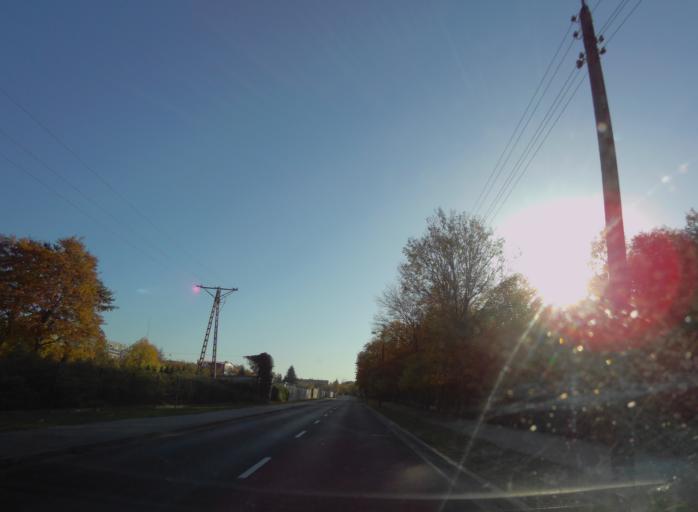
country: PL
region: Masovian Voivodeship
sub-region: Powiat pruszkowski
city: Granica
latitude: 52.1525
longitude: 20.7851
